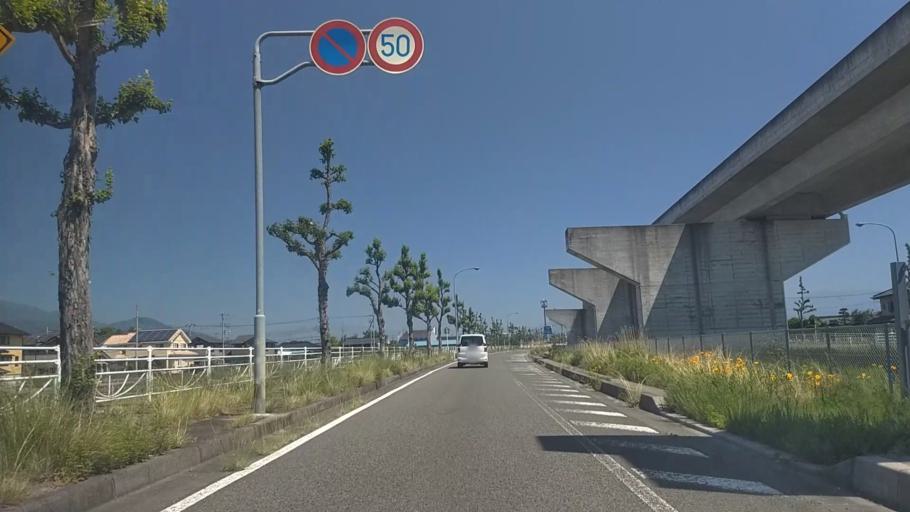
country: JP
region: Yamanashi
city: Ryuo
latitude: 35.5860
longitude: 138.4744
